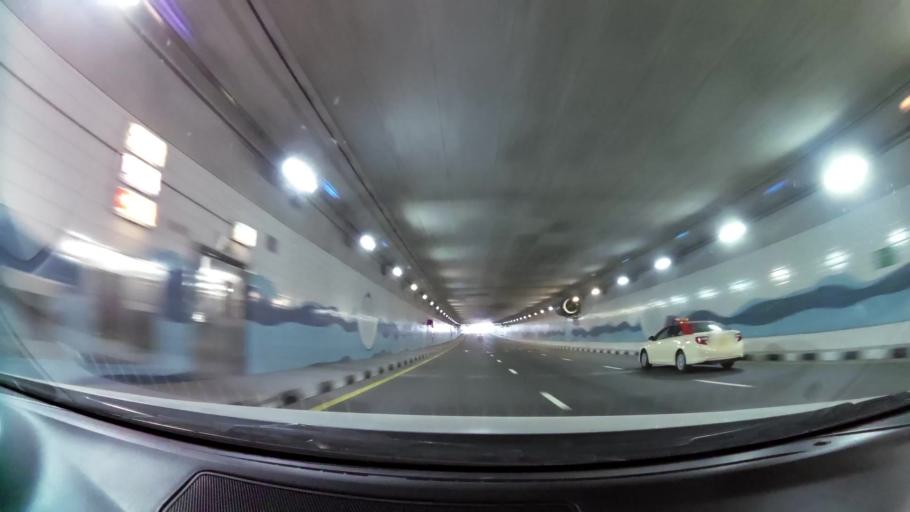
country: AE
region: Dubai
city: Dubai
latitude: 25.1256
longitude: 55.1156
